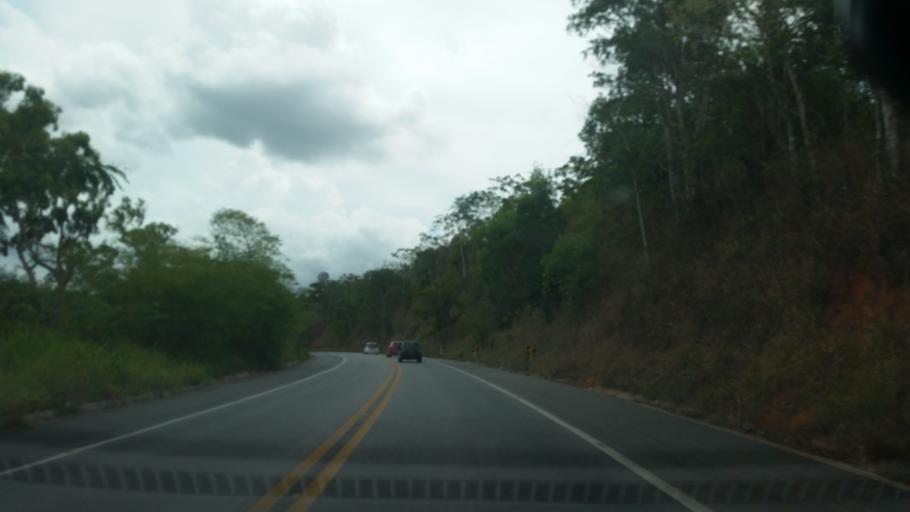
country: BR
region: Alagoas
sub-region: Uniao Dos Palmares
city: Uniao dos Palmares
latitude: -9.1928
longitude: -36.0359
